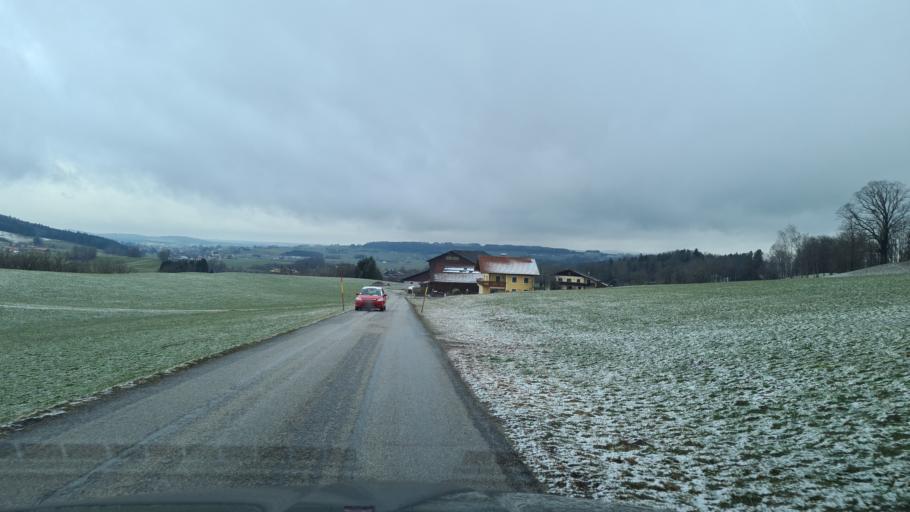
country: AT
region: Upper Austria
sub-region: Politischer Bezirk Vocklabruck
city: Oberhofen am Irrsee
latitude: 47.9491
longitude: 13.3146
